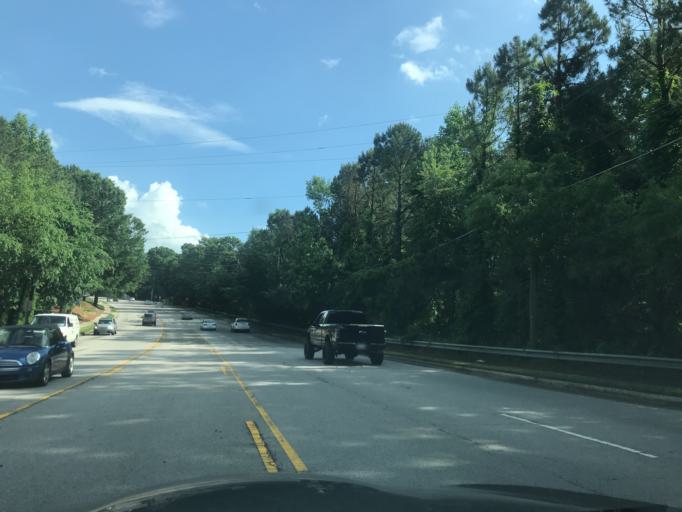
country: US
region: North Carolina
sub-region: Wake County
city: West Raleigh
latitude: 35.8775
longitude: -78.6456
